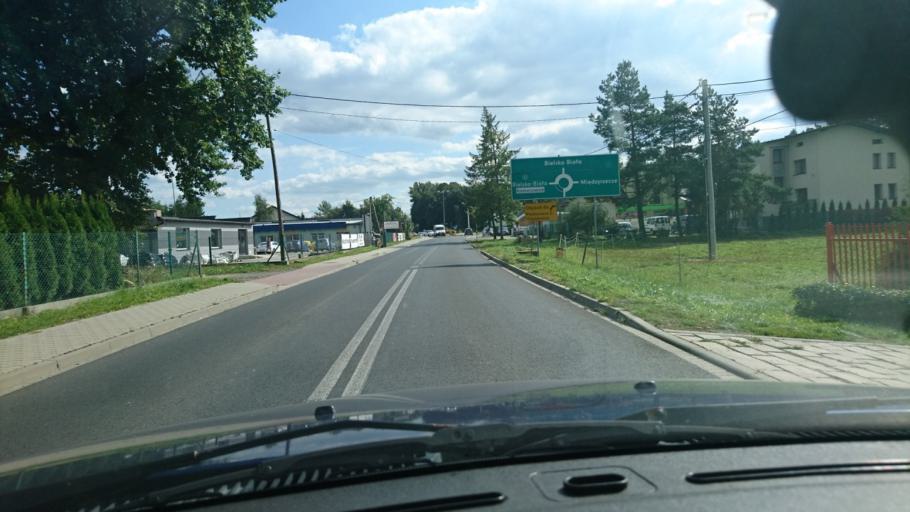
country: PL
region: Silesian Voivodeship
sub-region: Powiat bielski
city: Mazancowice
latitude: 49.8591
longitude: 18.9764
